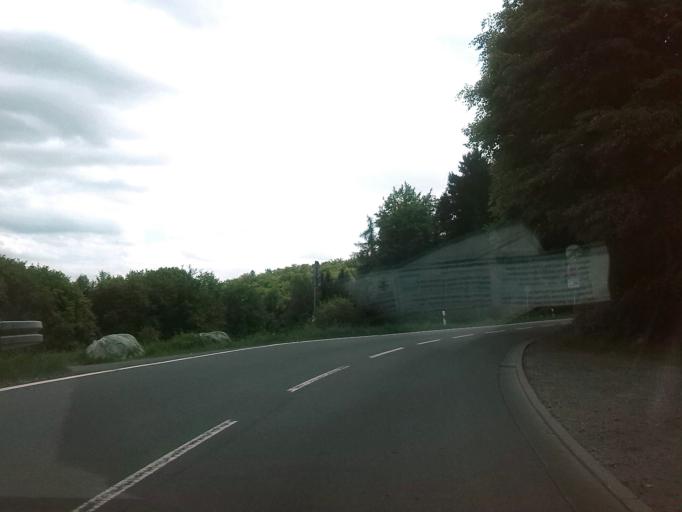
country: DE
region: Hesse
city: Lutzelbach
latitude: 49.7304
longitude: 8.7794
